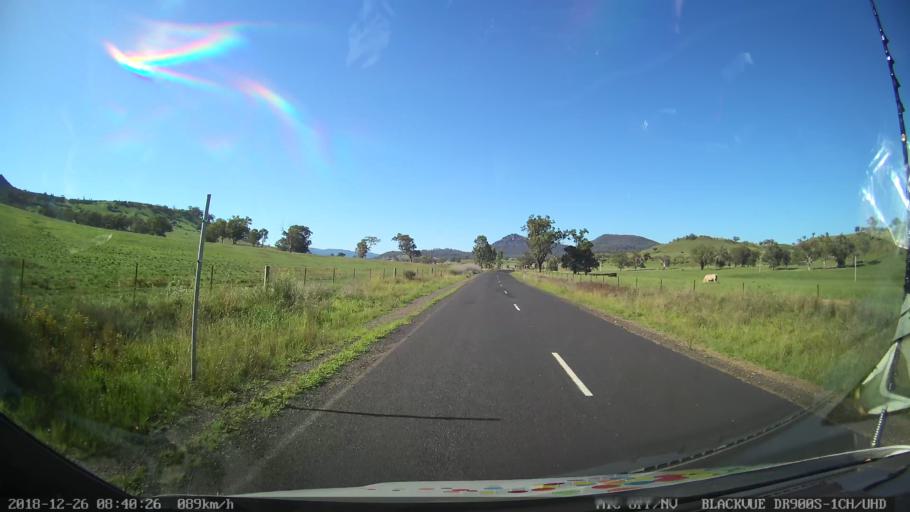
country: AU
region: New South Wales
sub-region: Mid-Western Regional
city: Kandos
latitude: -32.4668
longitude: 150.0762
